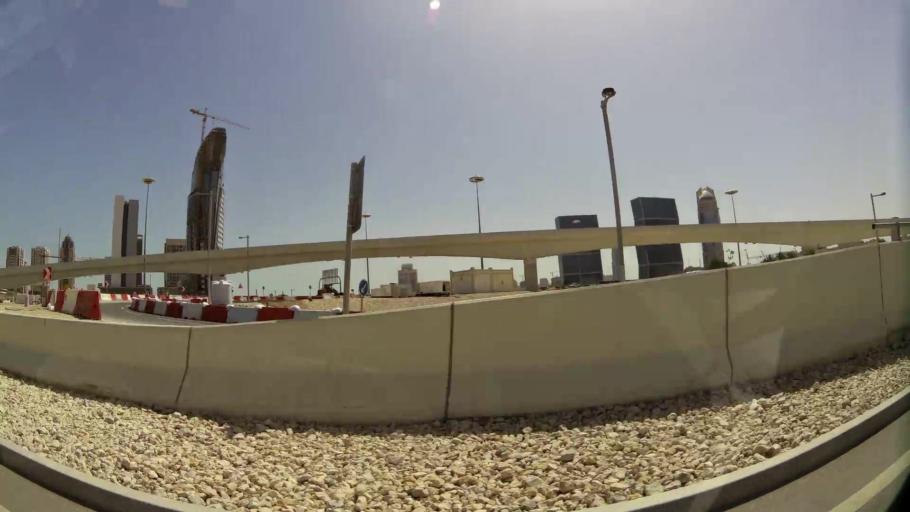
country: QA
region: Baladiyat ad Dawhah
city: Doha
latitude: 25.3823
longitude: 51.5197
